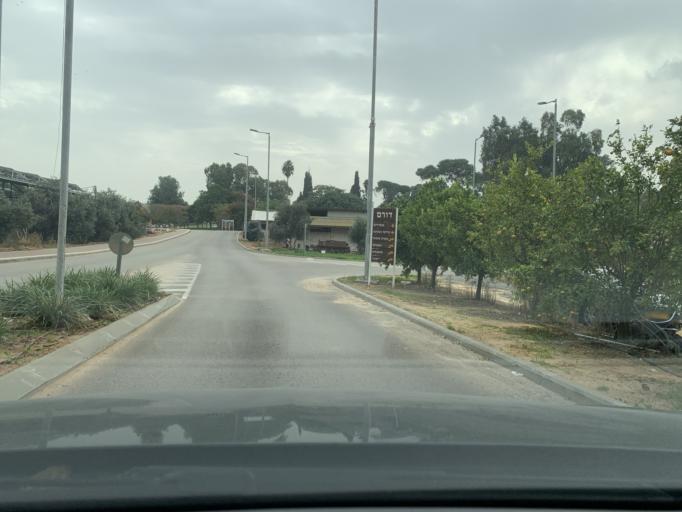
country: IL
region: Central District
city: Tirah
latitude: 32.2203
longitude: 34.9392
